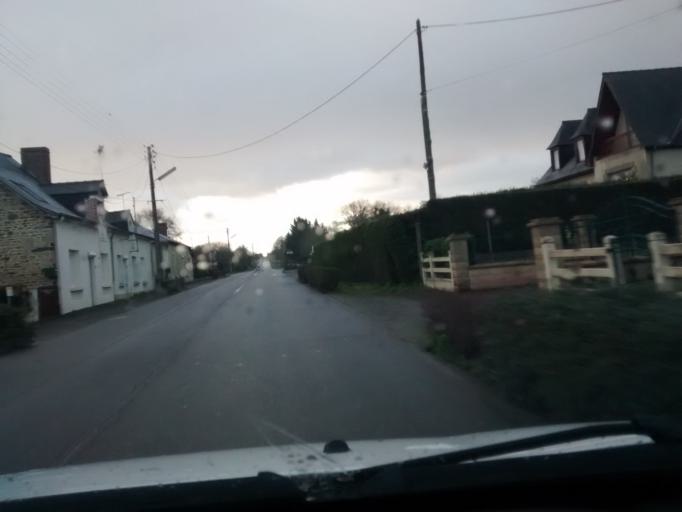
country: FR
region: Brittany
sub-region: Departement d'Ille-et-Vilaine
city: Bais
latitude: 48.0044
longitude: -1.2887
